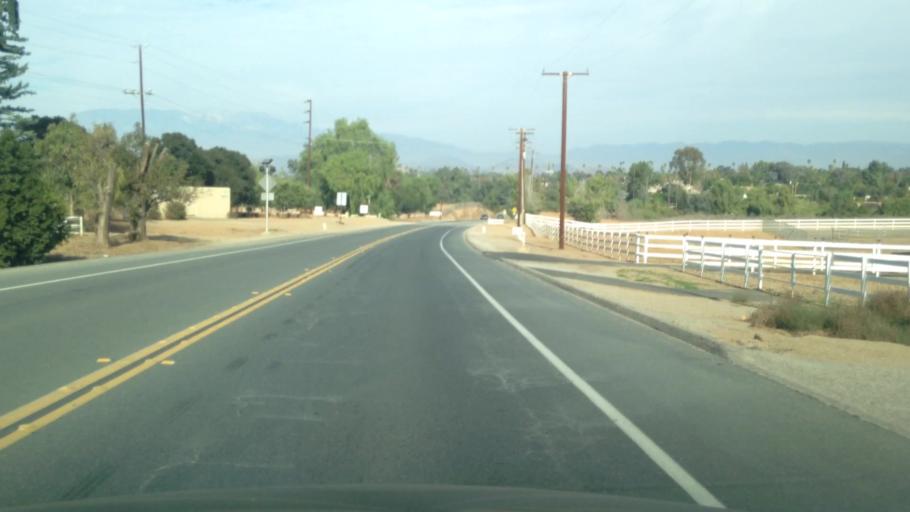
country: US
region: California
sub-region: Riverside County
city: Woodcrest
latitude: 33.9003
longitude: -117.3830
